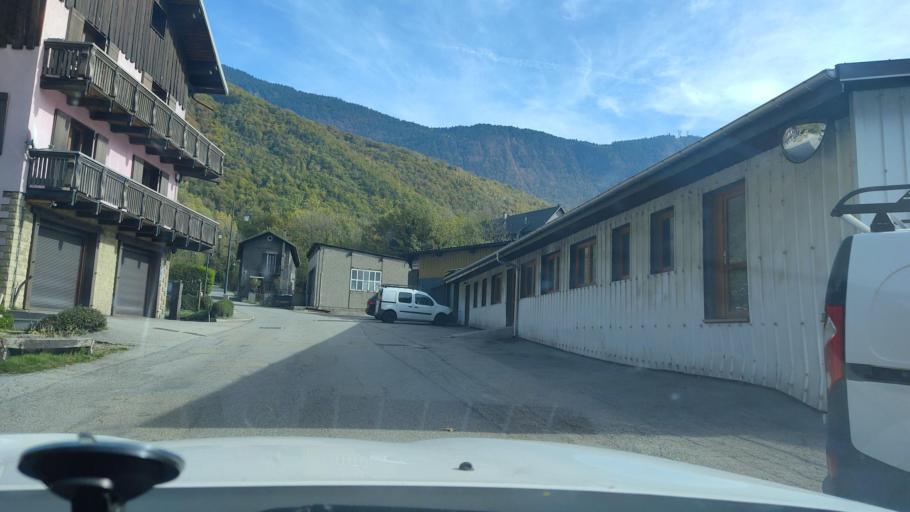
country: FR
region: Rhone-Alpes
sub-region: Departement de la Savoie
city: Aigueblanche
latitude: 45.5248
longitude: 6.4858
